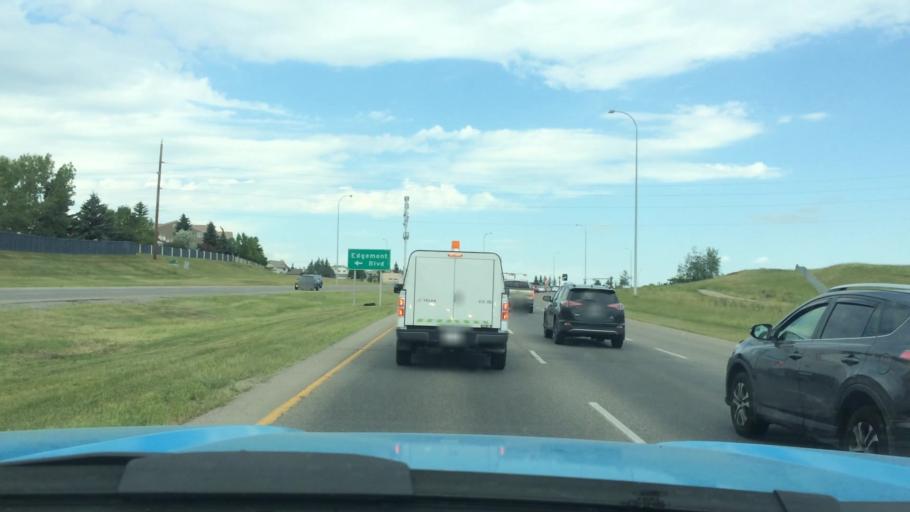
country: CA
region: Alberta
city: Calgary
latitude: 51.1239
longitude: -114.1343
